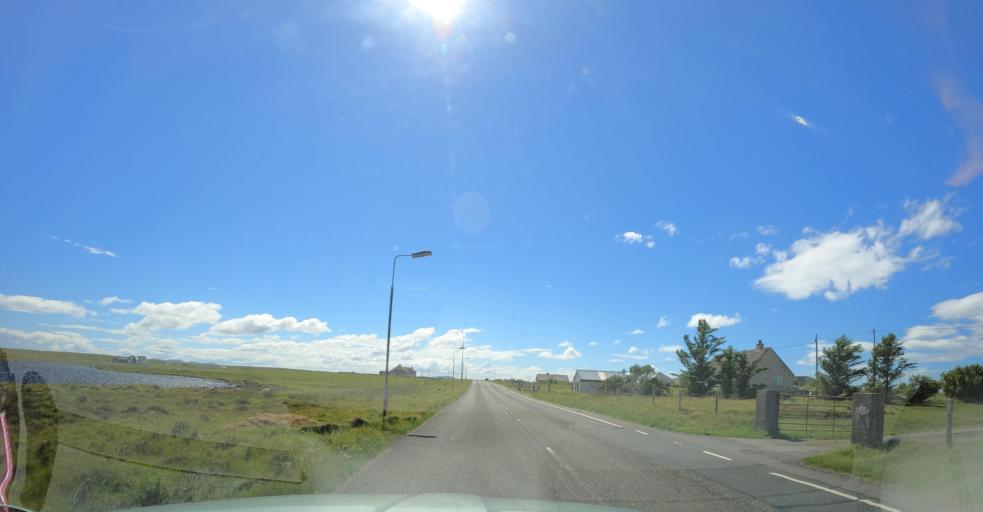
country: GB
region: Scotland
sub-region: Eilean Siar
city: Isle of Lewis
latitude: 58.4020
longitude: -6.4653
